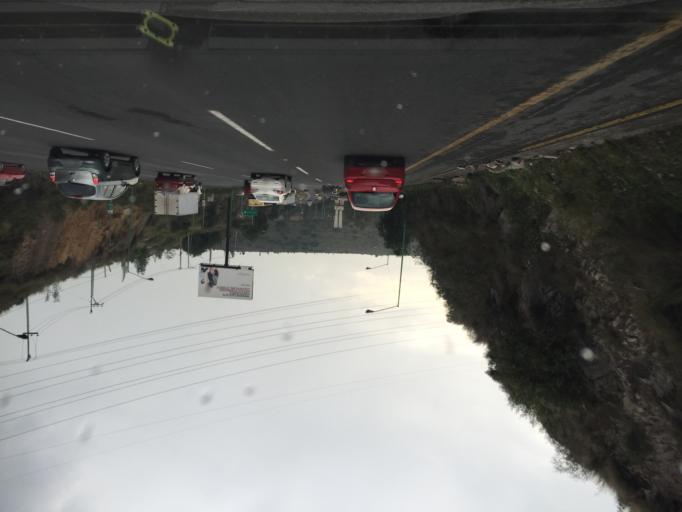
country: MX
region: Mexico
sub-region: Tultitlan
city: Buenavista
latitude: 19.5985
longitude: -99.1961
